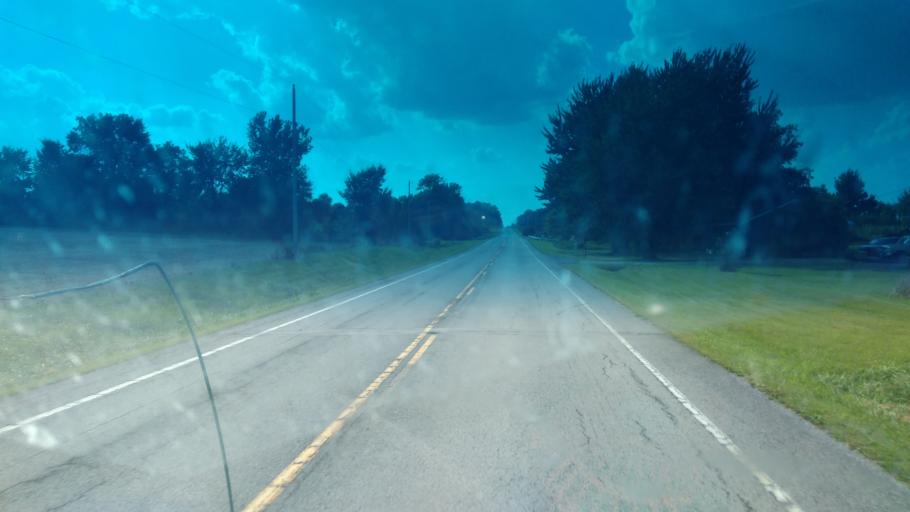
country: US
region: Ohio
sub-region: Hardin County
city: Forest
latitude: 40.8333
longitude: -83.5712
